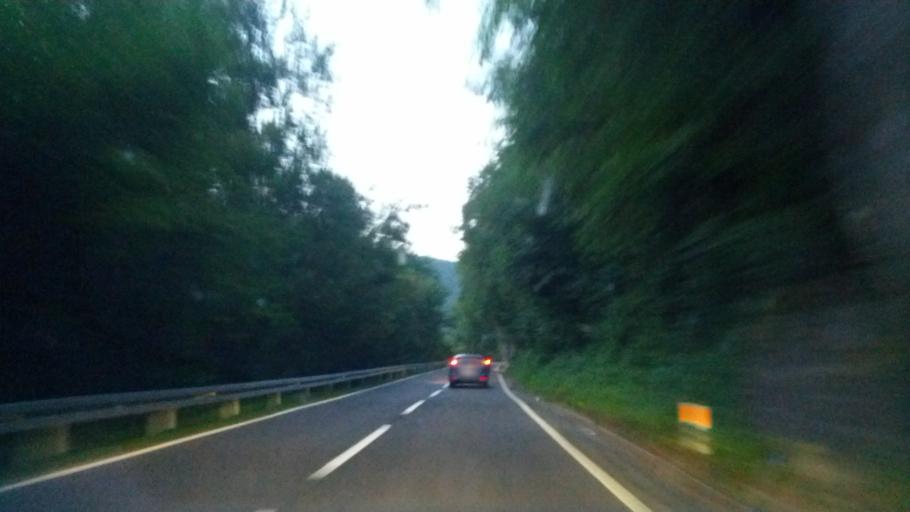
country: BA
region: Federation of Bosnia and Herzegovina
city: Bosanska Krupa
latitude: 44.8721
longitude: 16.1116
